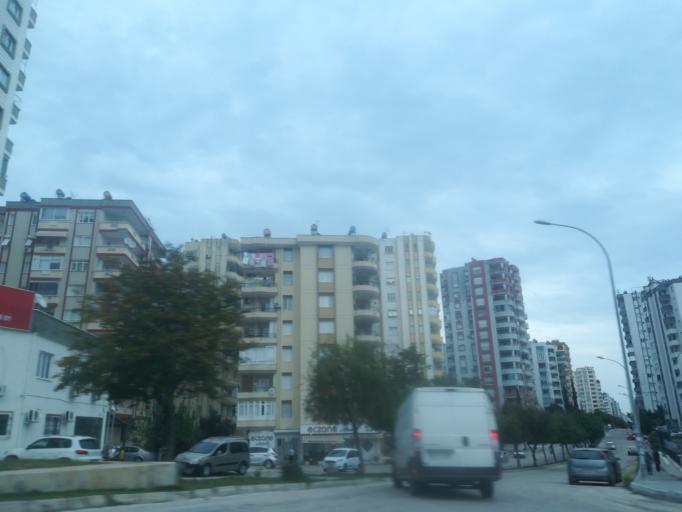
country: TR
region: Adana
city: Adana
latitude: 37.0430
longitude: 35.2916
